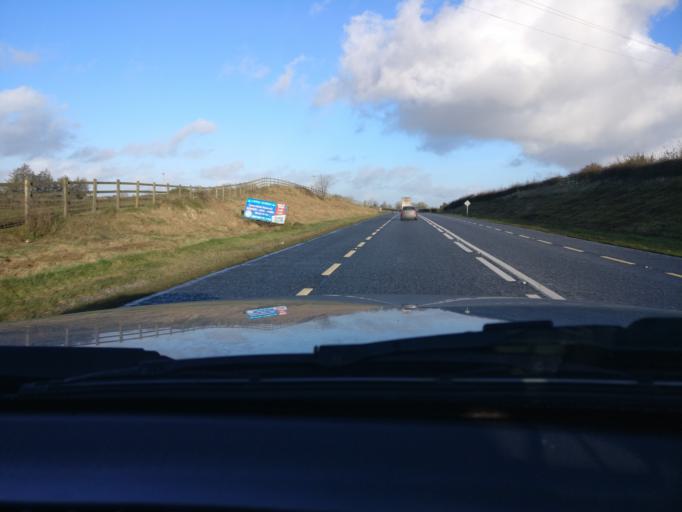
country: IE
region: Leinster
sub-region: An Iarmhi
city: Rathwire
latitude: 53.5975
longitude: -7.1102
